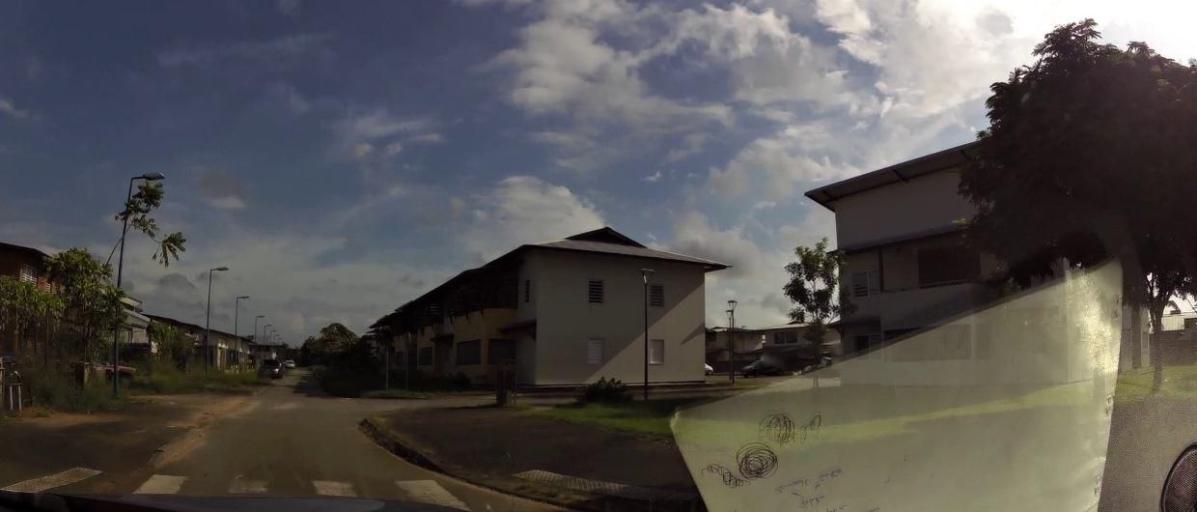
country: GF
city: Macouria
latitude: 4.9218
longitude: -52.4171
